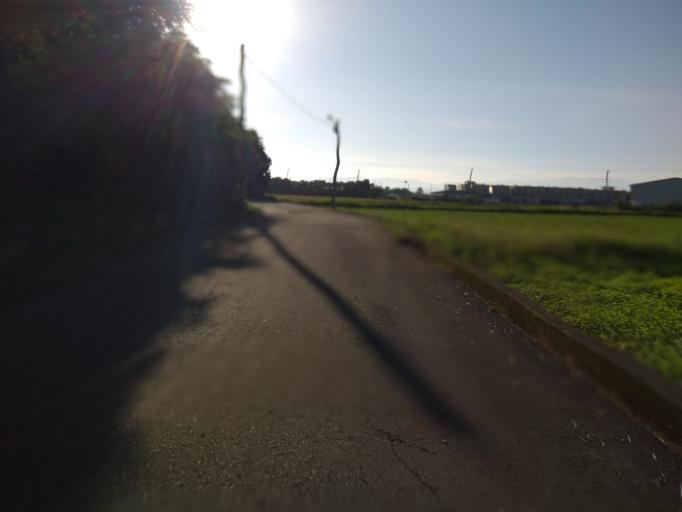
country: TW
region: Taiwan
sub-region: Hsinchu
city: Zhubei
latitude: 24.9953
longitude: 121.0504
